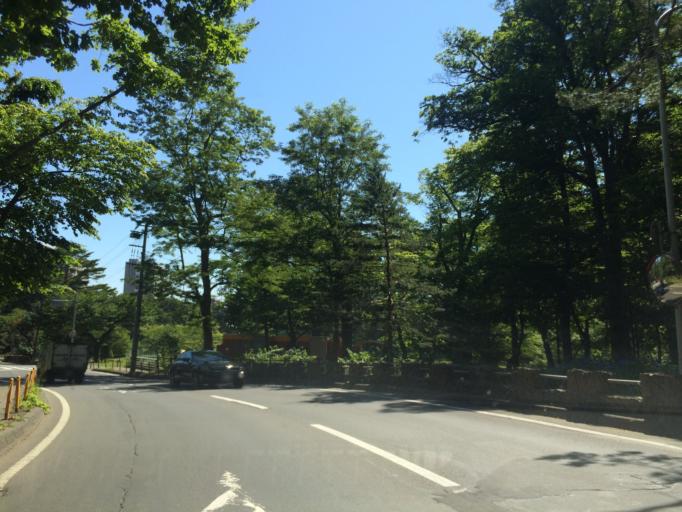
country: JP
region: Hokkaido
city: Sapporo
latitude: 43.0533
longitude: 141.3126
